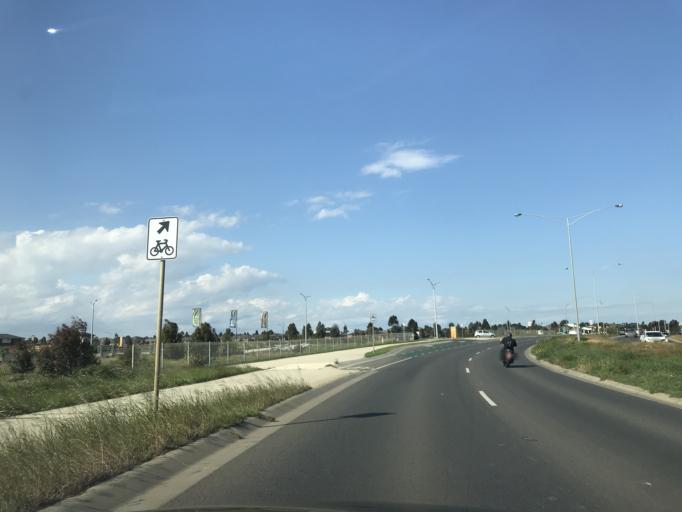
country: AU
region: Victoria
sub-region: Wyndham
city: Hoppers Crossing
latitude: -37.8961
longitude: 144.7144
